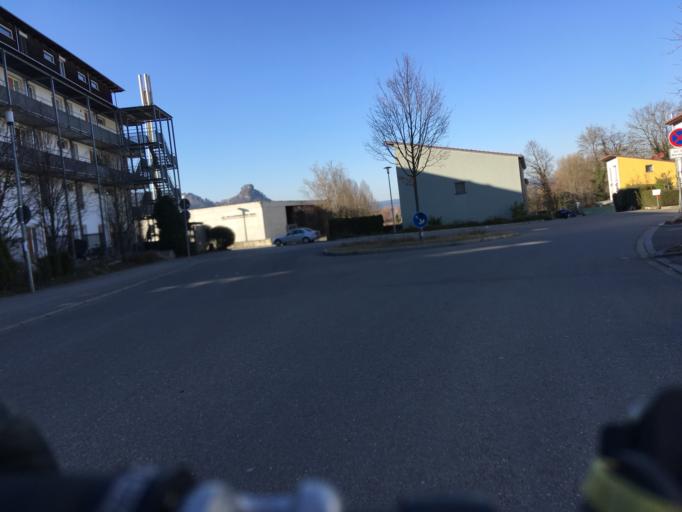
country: DE
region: Baden-Wuerttemberg
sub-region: Freiburg Region
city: Singen
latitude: 47.7783
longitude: 8.8400
